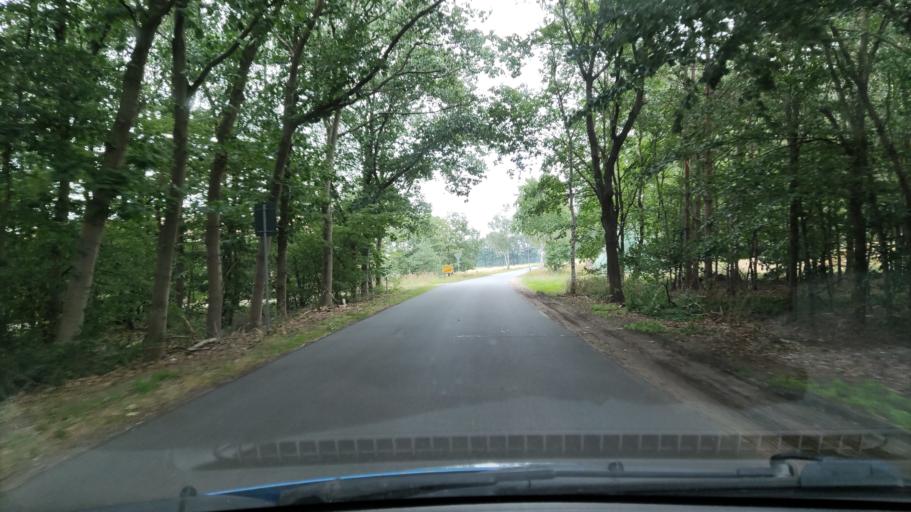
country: DE
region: Lower Saxony
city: Rosche
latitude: 53.0151
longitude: 10.7321
